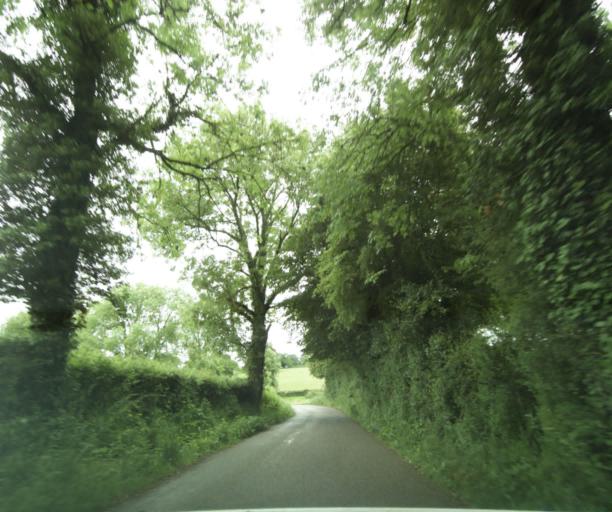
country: FR
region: Bourgogne
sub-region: Departement de Saone-et-Loire
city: Charolles
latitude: 46.4360
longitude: 4.3444
